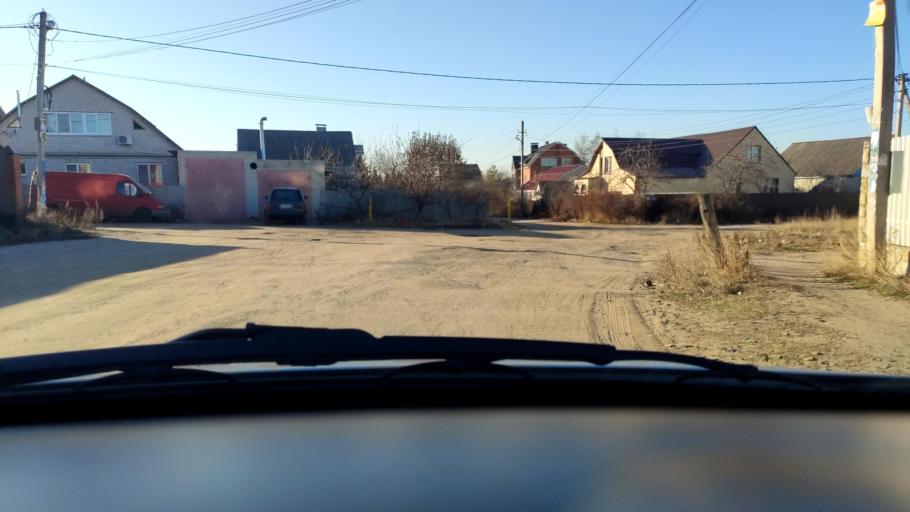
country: RU
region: Voronezj
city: Podgornoye
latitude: 51.7258
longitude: 39.1555
